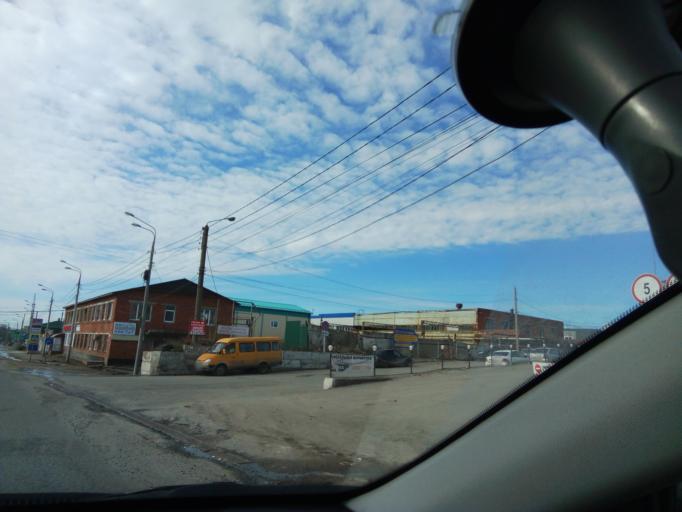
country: RU
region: Chuvashia
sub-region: Cheboksarskiy Rayon
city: Cheboksary
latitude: 56.1058
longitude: 47.2497
